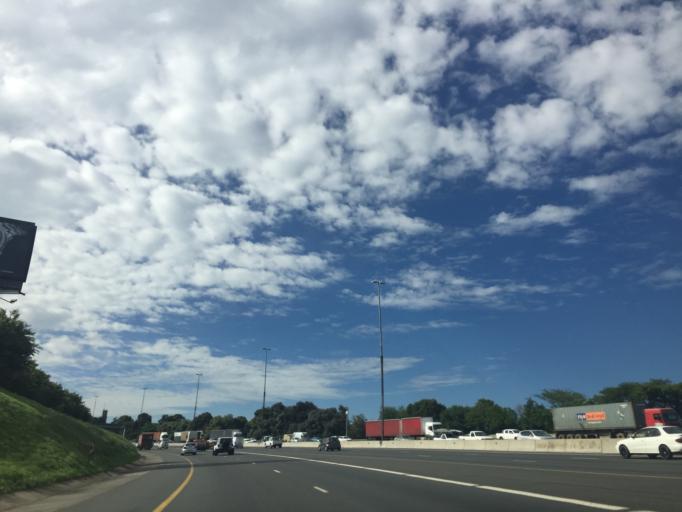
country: ZA
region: Gauteng
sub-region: Ekurhuleni Metropolitan Municipality
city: Germiston
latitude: -26.1746
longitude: 28.1315
